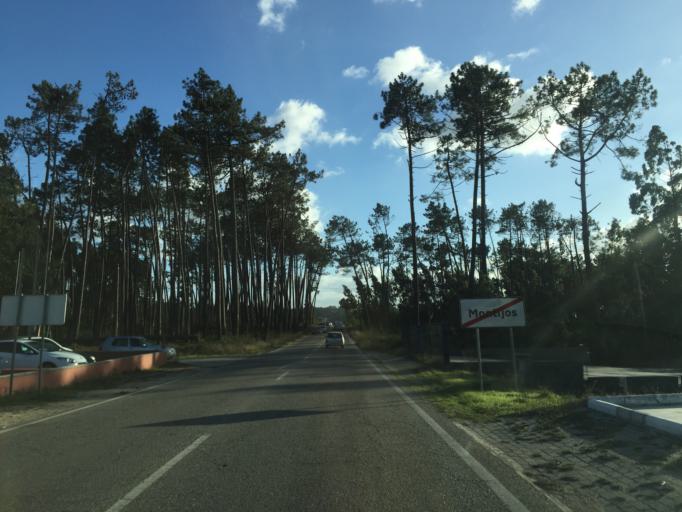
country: PT
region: Leiria
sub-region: Leiria
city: Monte Redondo
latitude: 39.8756
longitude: -8.8387
